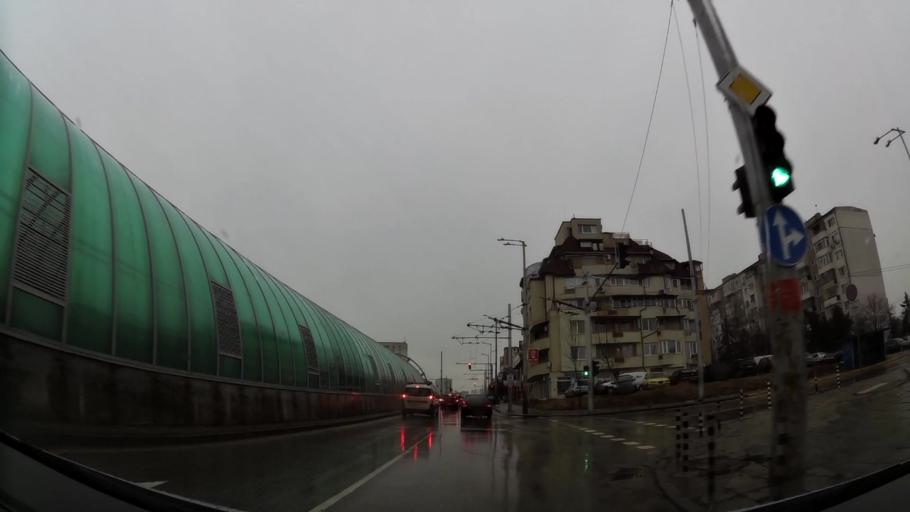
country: BG
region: Sofia-Capital
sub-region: Stolichna Obshtina
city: Sofia
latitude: 42.6551
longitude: 23.3701
